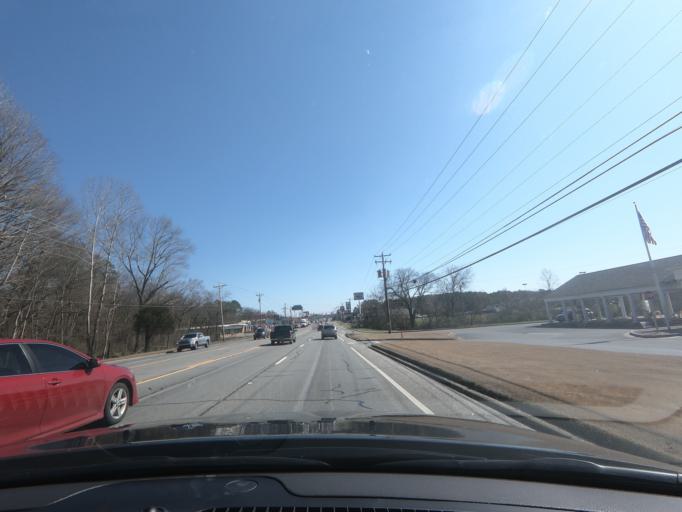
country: US
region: Georgia
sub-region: Gordon County
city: Calhoun
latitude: 34.4767
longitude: -84.9307
